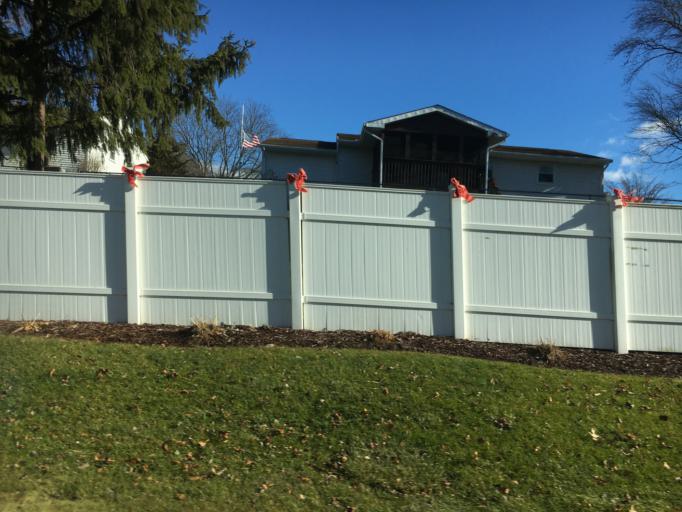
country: US
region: Pennsylvania
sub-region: Lehigh County
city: Stiles
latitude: 40.6347
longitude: -75.5082
